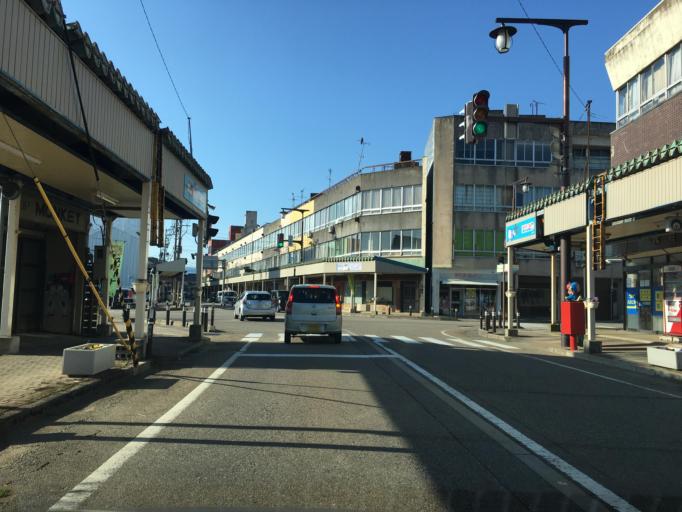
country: JP
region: Toyama
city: Himi
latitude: 36.8591
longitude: 136.9871
